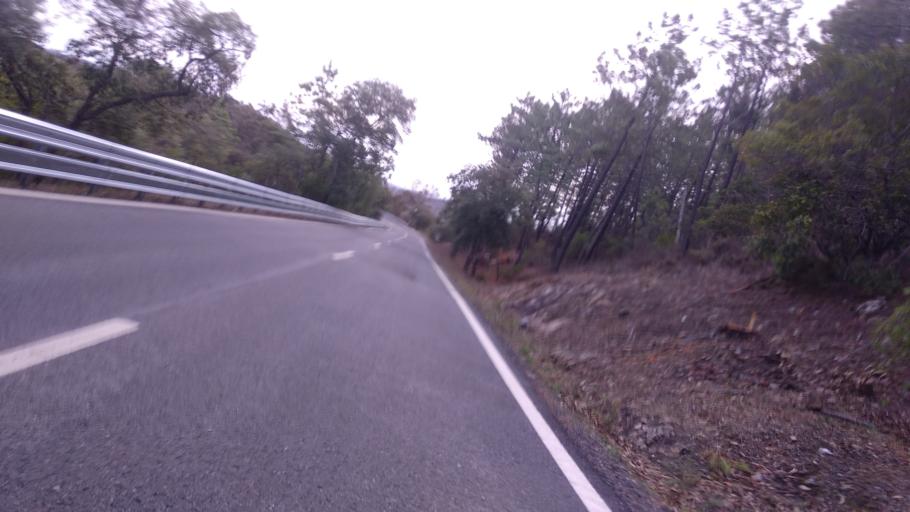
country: PT
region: Faro
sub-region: Sao Bras de Alportel
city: Sao Bras de Alportel
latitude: 37.1815
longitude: -7.9189
